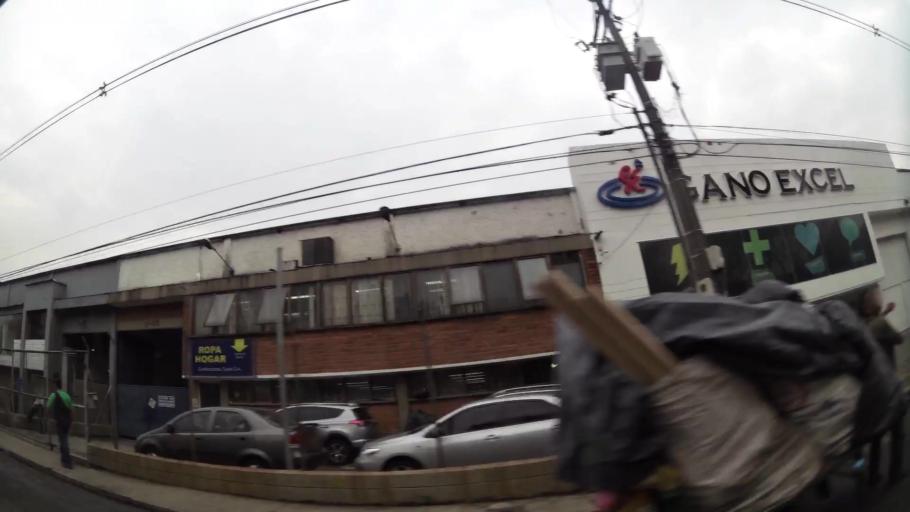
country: CO
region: Antioquia
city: Medellin
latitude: 6.2225
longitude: -75.5716
